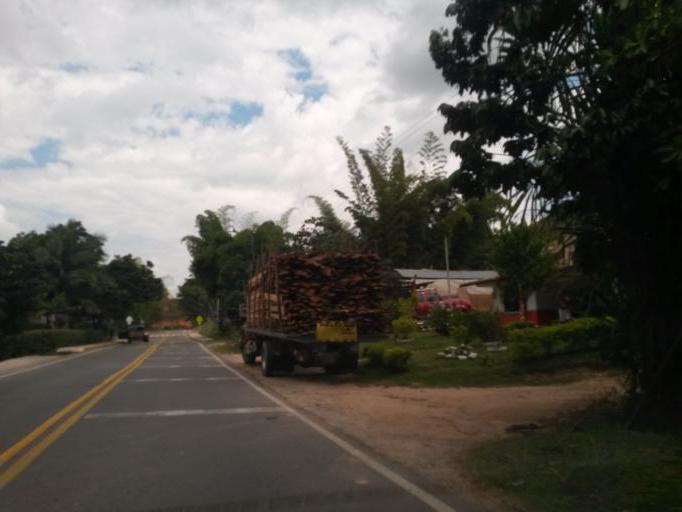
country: CO
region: Cauca
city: Lopez
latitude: 2.4786
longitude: -76.7147
